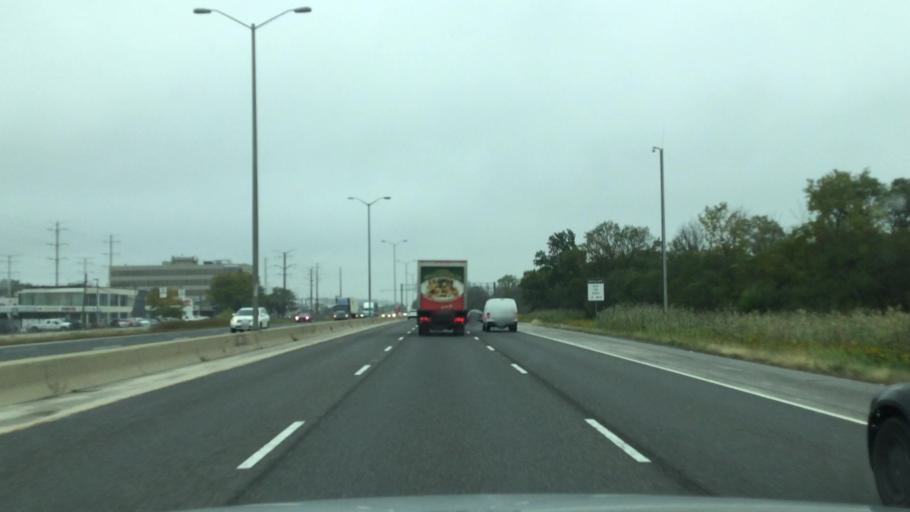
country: US
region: Illinois
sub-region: Cook County
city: Northfield
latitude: 42.1227
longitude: -87.7815
